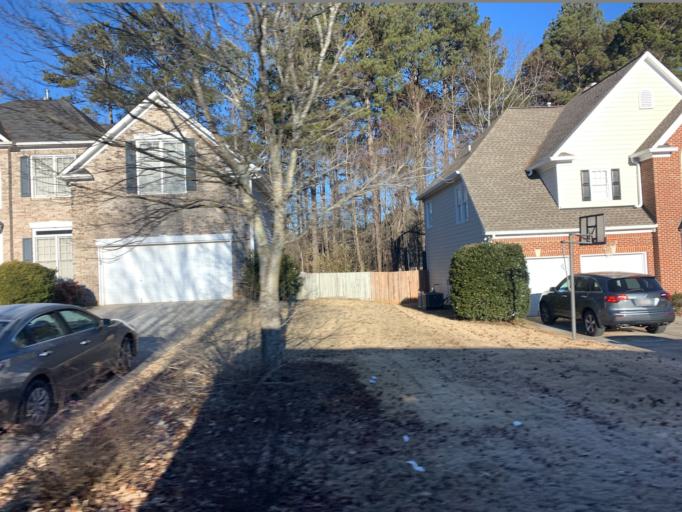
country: US
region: Georgia
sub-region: Gwinnett County
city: Mountain Park
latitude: 33.8629
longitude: -84.1086
